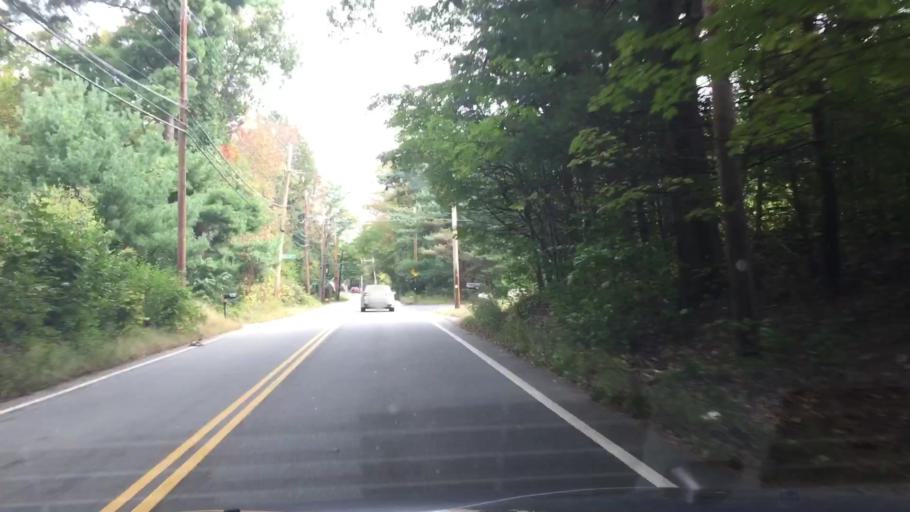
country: US
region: Massachusetts
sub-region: Essex County
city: Methuen
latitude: 42.6764
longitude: -71.2232
